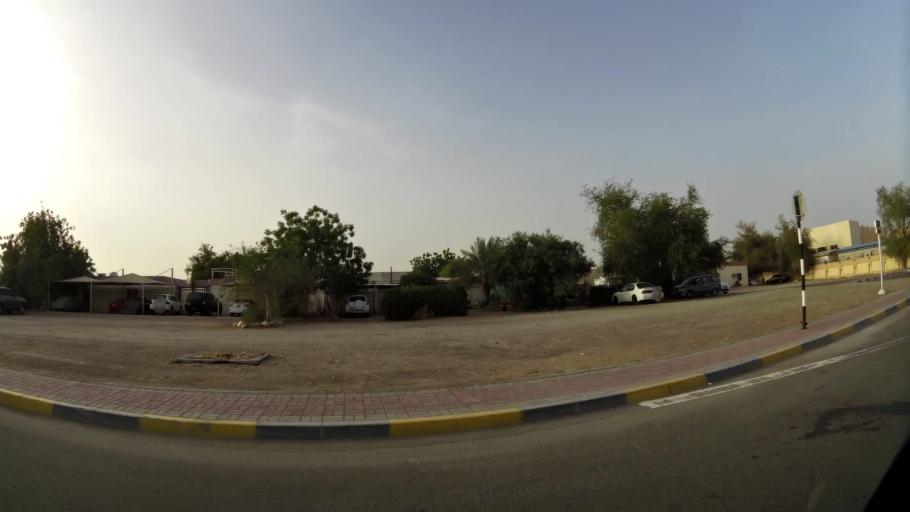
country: OM
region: Al Buraimi
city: Al Buraymi
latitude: 24.2441
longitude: 55.7445
